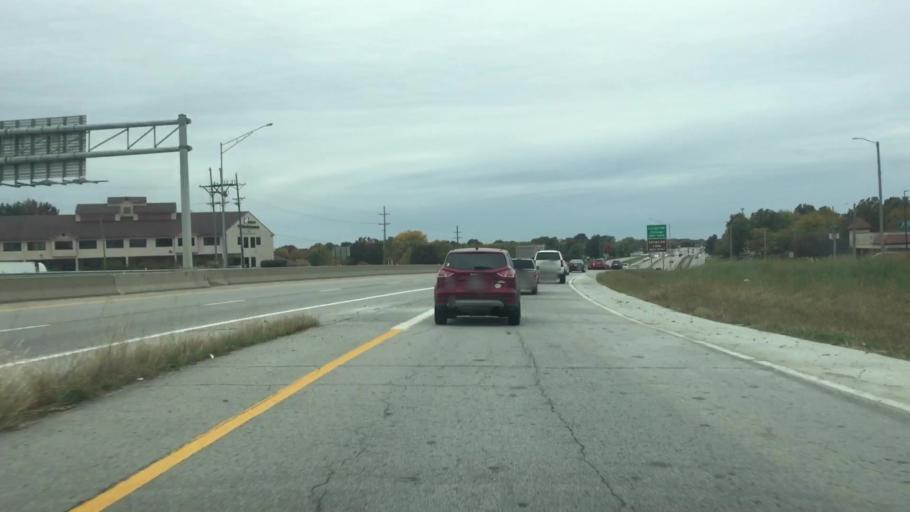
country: US
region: Missouri
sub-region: Jackson County
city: Lees Summit
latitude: 38.9041
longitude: -94.3797
